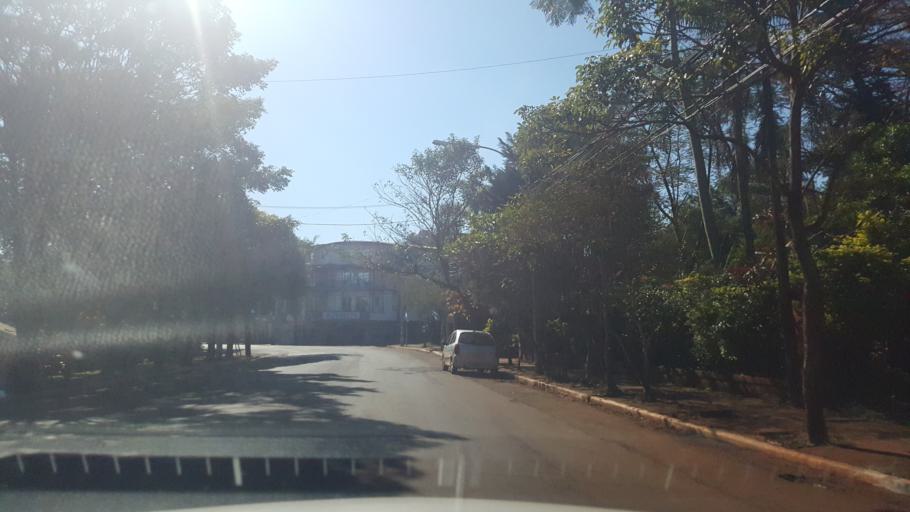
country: AR
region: Misiones
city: Puerto Rico
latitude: -26.8198
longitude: -55.0273
